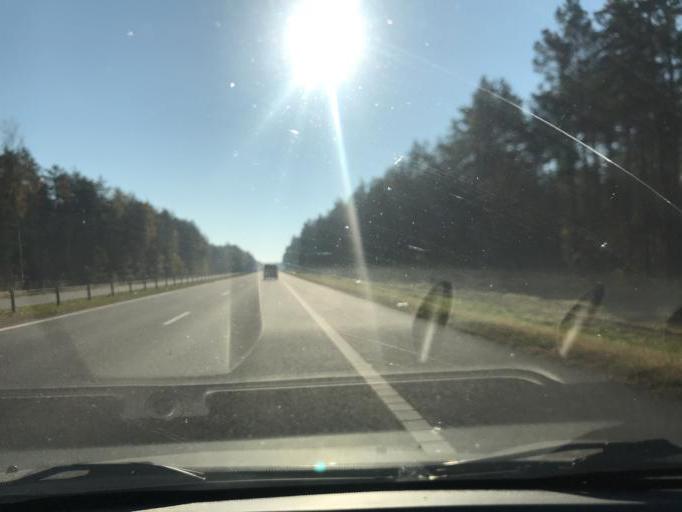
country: BY
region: Minsk
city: Pukhavichy
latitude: 53.4712
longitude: 28.3834
